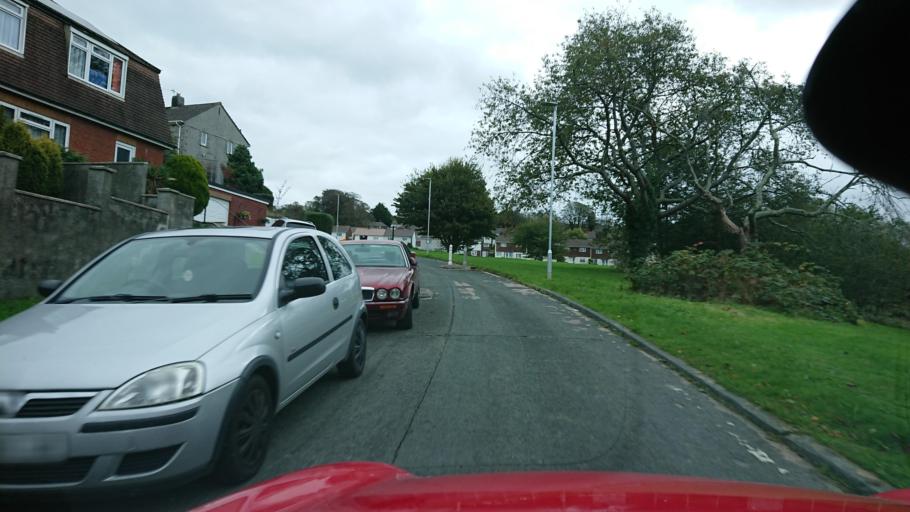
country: GB
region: England
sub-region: Plymouth
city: Plymouth
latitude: 50.4135
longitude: -4.1399
